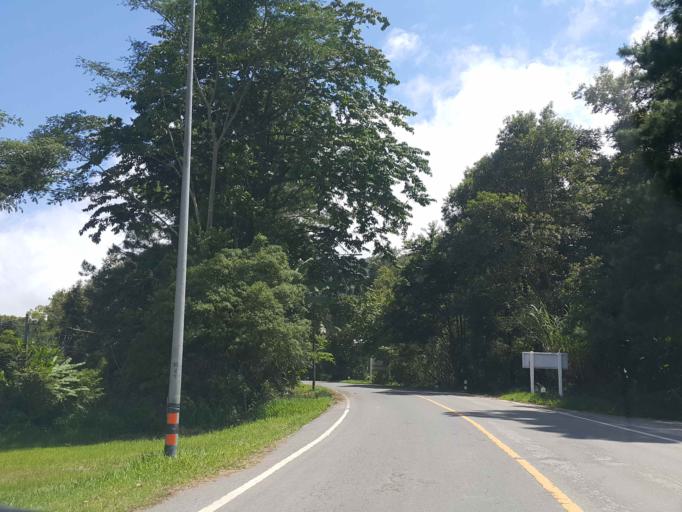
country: TH
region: Chiang Mai
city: Mae Chaem
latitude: 18.5353
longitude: 98.5223
